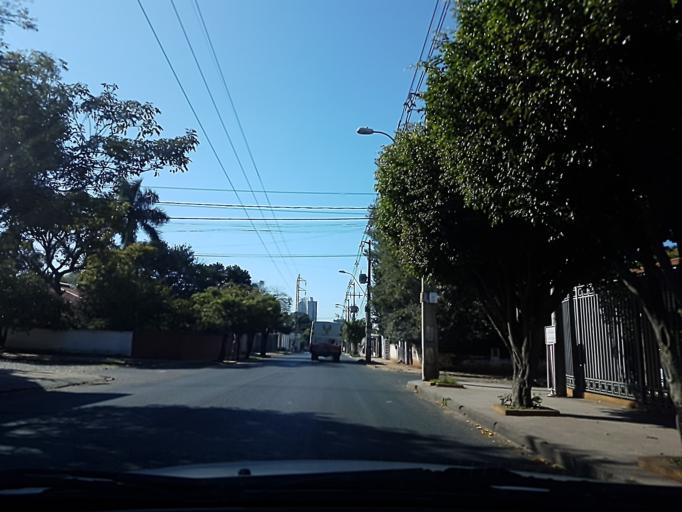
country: PY
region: Central
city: Fernando de la Mora
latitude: -25.2961
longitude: -57.5622
